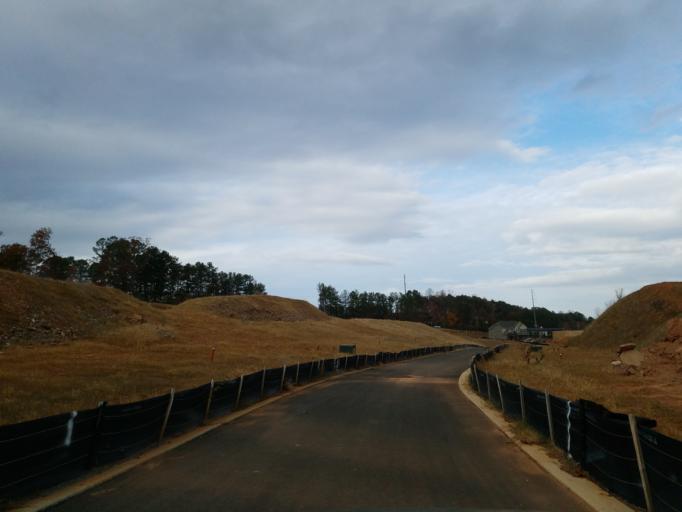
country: US
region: Georgia
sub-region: Cobb County
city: Fair Oaks
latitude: 33.8918
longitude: -84.5444
